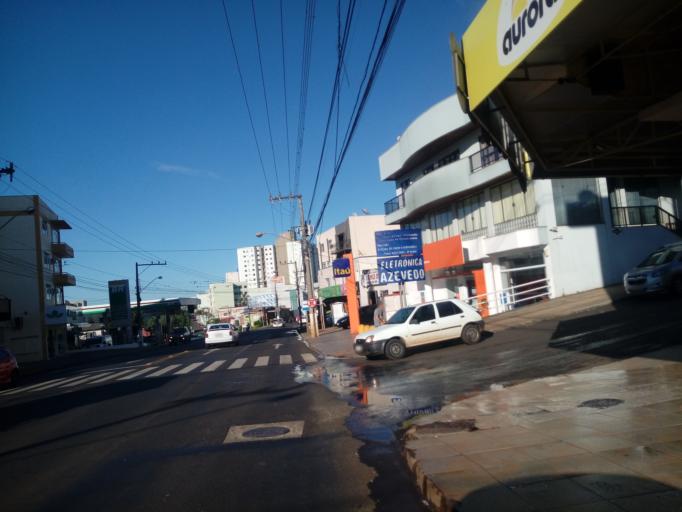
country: BR
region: Santa Catarina
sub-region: Chapeco
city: Chapeco
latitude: -27.0945
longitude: -52.6266
